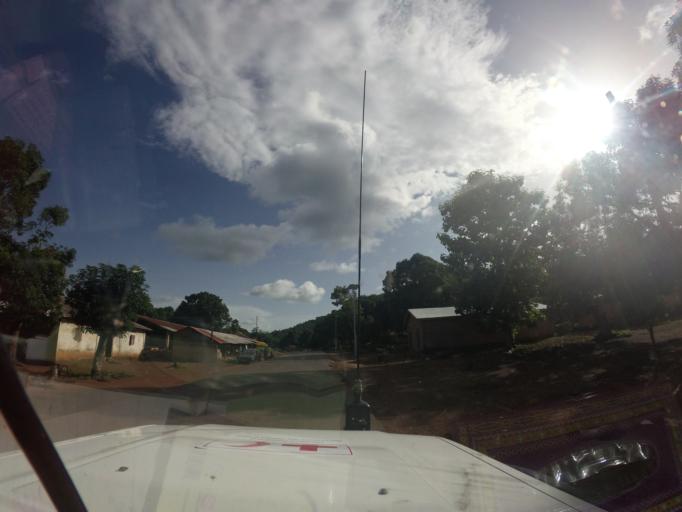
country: GN
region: Kindia
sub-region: Kindia
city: Kindia
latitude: 10.1565
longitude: -12.5350
